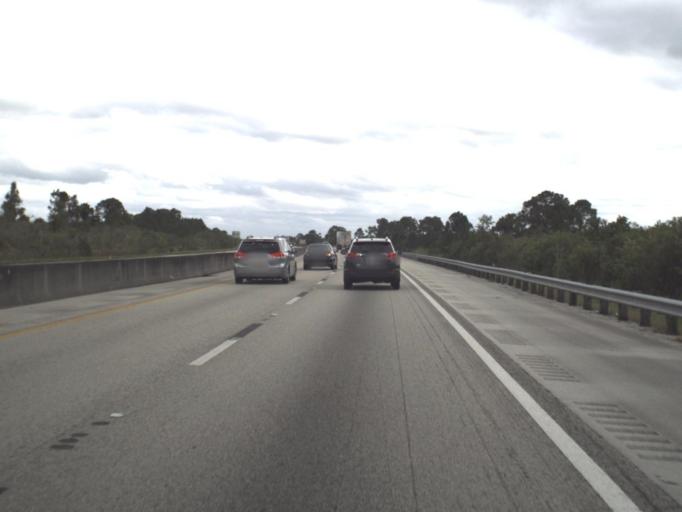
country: US
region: Florida
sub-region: Martin County
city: Hobe Sound
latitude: 27.0282
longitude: -80.2343
